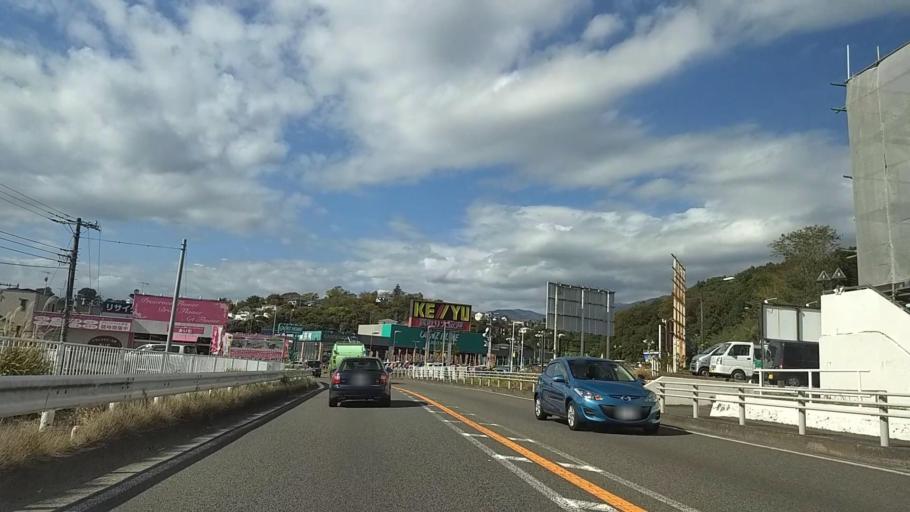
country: JP
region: Kanagawa
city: Hadano
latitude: 35.3810
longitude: 139.2303
